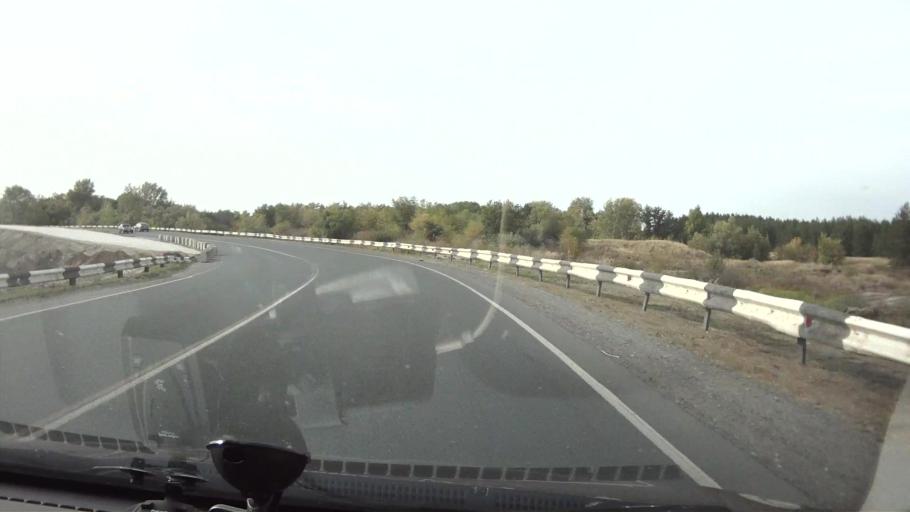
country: RU
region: Saratov
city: Sennoy
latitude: 52.1432
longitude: 46.9064
